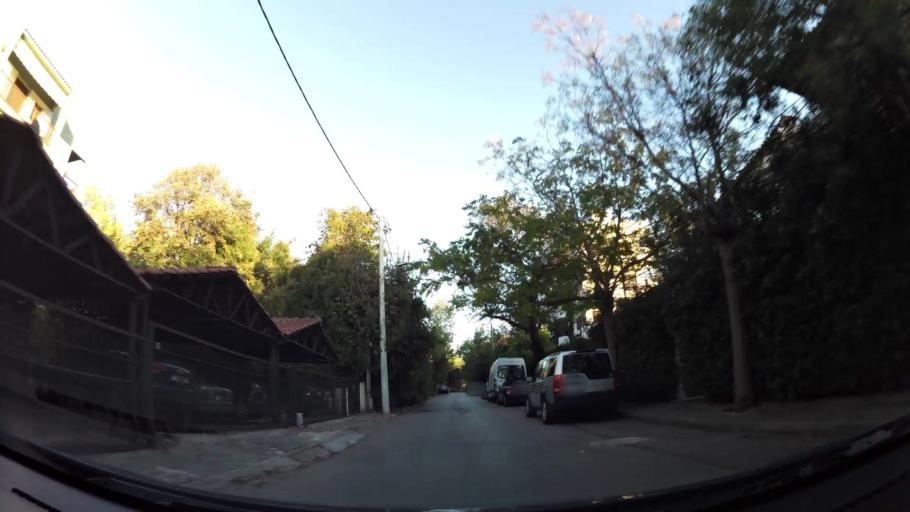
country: GR
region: Attica
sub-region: Nomarchia Athinas
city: Kifisia
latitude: 38.0845
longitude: 23.8204
